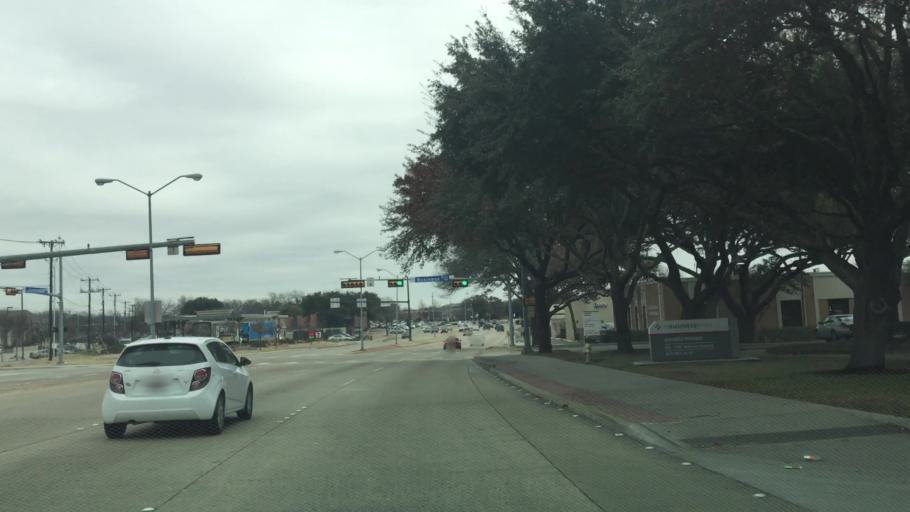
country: US
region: Texas
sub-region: Dallas County
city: Richardson
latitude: 32.9399
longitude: -96.7377
